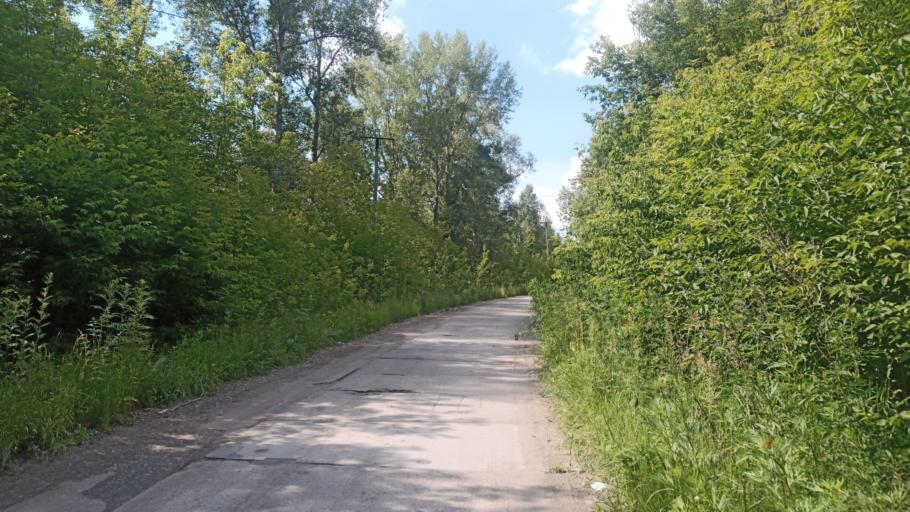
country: RU
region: Altai Krai
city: Zaton
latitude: 53.3380
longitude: 83.8066
